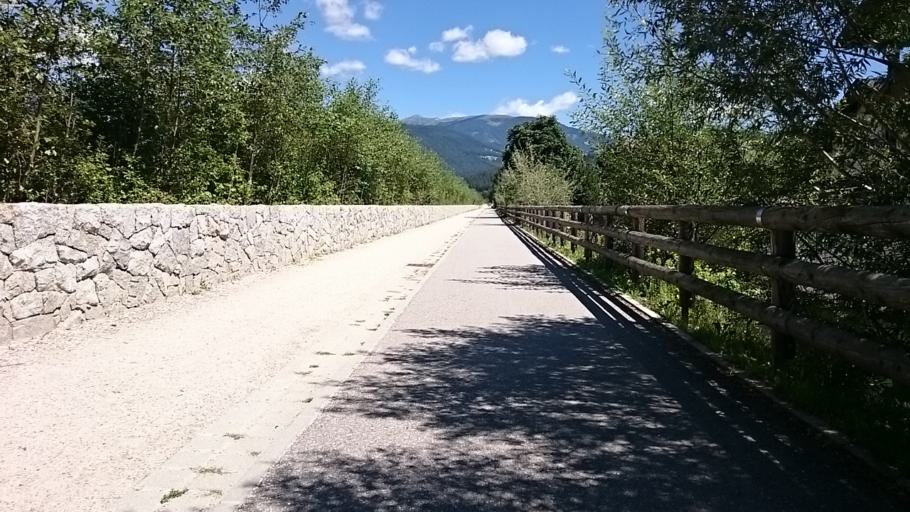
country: IT
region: Trentino-Alto Adige
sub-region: Bolzano
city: San Lorenzo di Sebato
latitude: 46.7870
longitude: 11.9106
